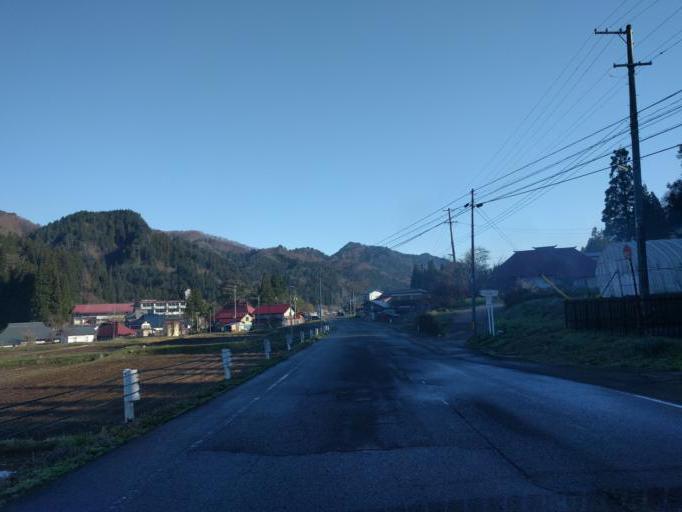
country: JP
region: Fukushima
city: Kitakata
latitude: 37.7164
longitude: 139.7817
